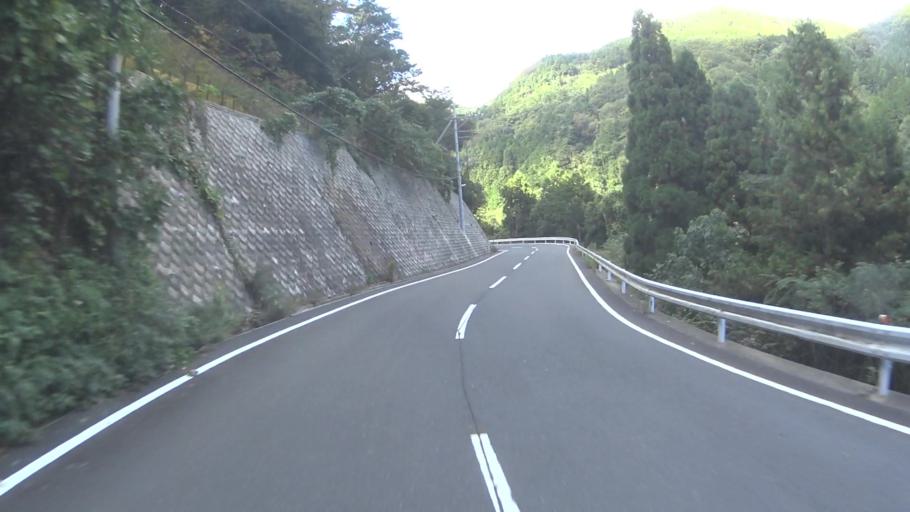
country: JP
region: Kyoto
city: Maizuru
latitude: 35.5560
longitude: 135.4391
